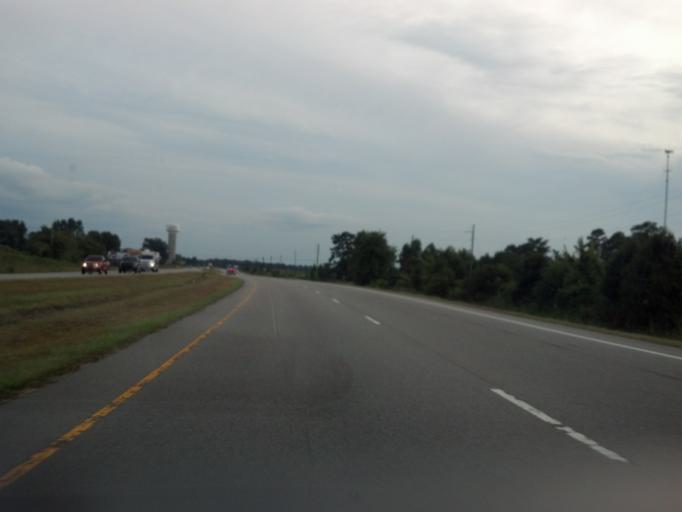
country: US
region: North Carolina
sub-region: Pitt County
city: Ayden
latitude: 35.4939
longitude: -77.4278
